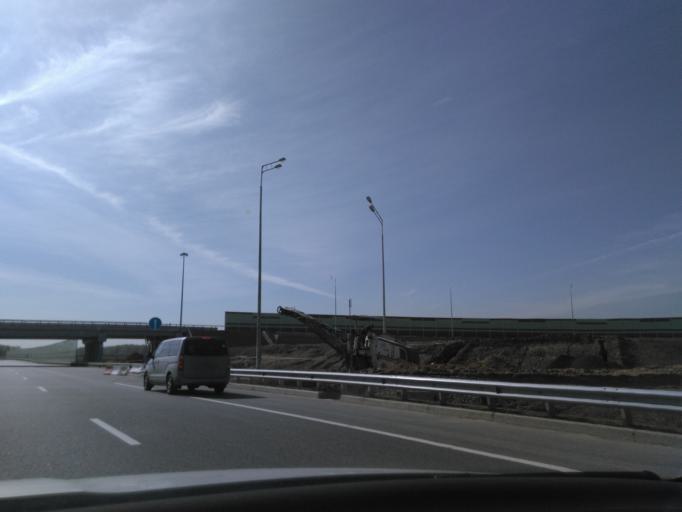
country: RU
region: Moskovskaya
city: Novopodrezkovo
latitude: 55.9576
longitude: 37.3658
